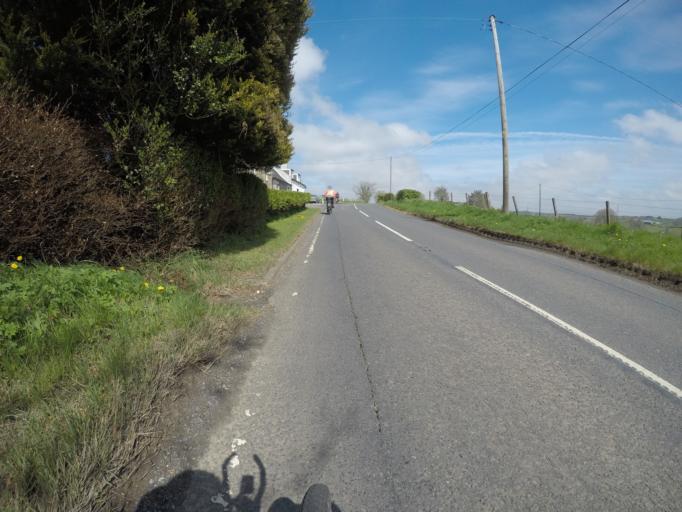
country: GB
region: Scotland
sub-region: East Ayrshire
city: Stewarton
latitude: 55.6947
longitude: -4.4907
